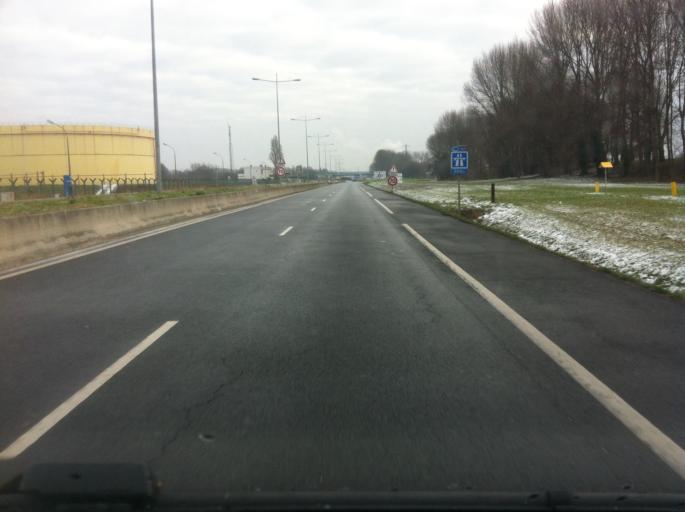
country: FR
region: Haute-Normandie
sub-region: Departement de la Seine-Maritime
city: Rogerville
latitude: 49.4800
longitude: 0.2544
